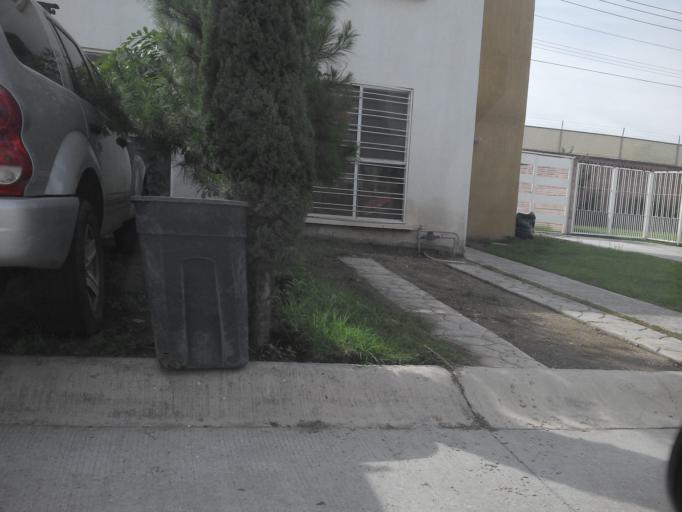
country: MX
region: Jalisco
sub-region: San Pedro Tlaquepaque
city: Paseo del Prado
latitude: 20.5760
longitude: -103.3898
